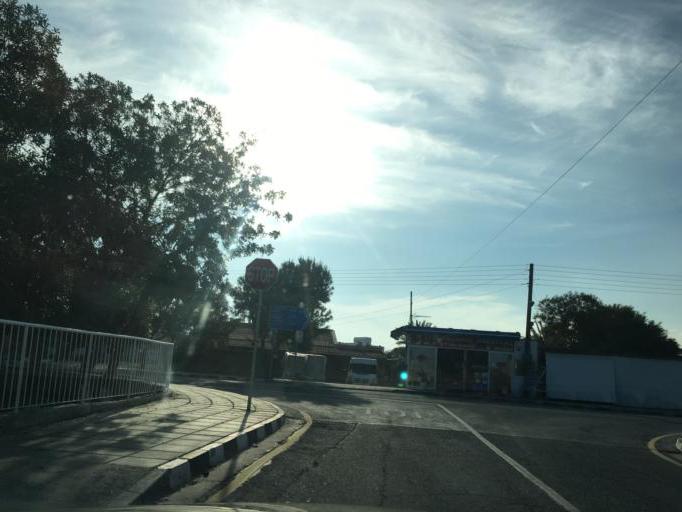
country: CY
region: Larnaka
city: Kofinou
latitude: 34.7286
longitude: 33.3356
